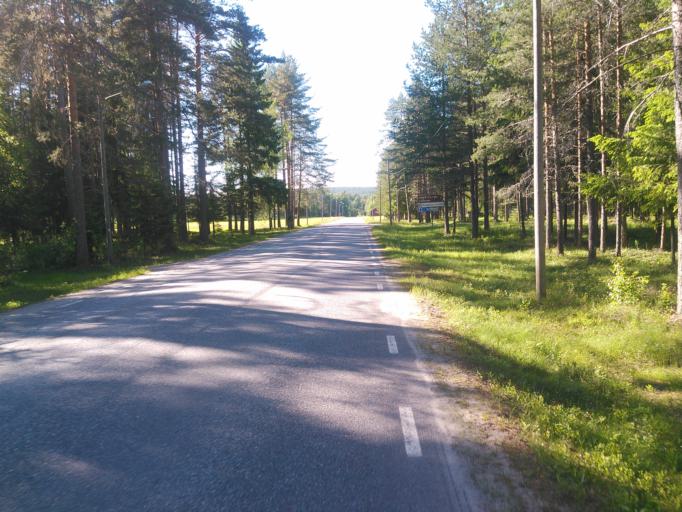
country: SE
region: Vaesterbotten
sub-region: Umea Kommun
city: Roback
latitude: 63.8316
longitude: 20.1103
